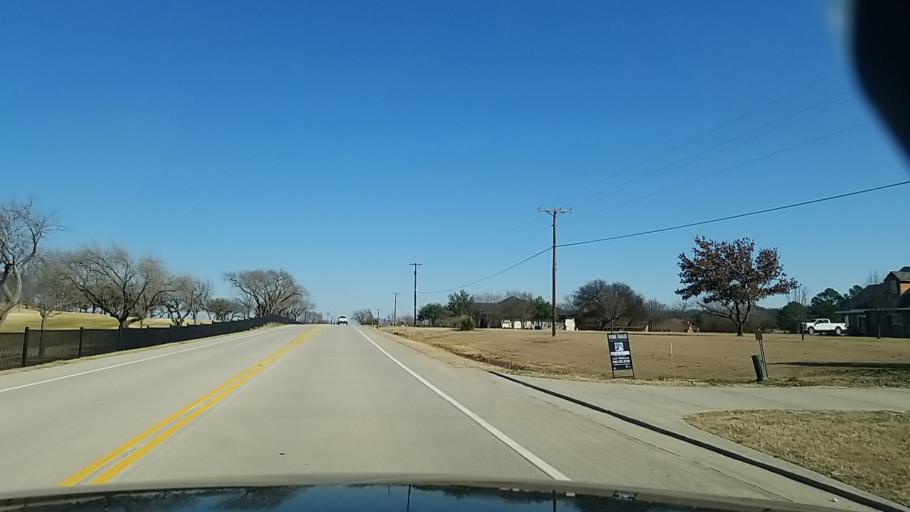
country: US
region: Texas
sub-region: Denton County
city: Argyle
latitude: 33.1388
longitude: -97.1603
